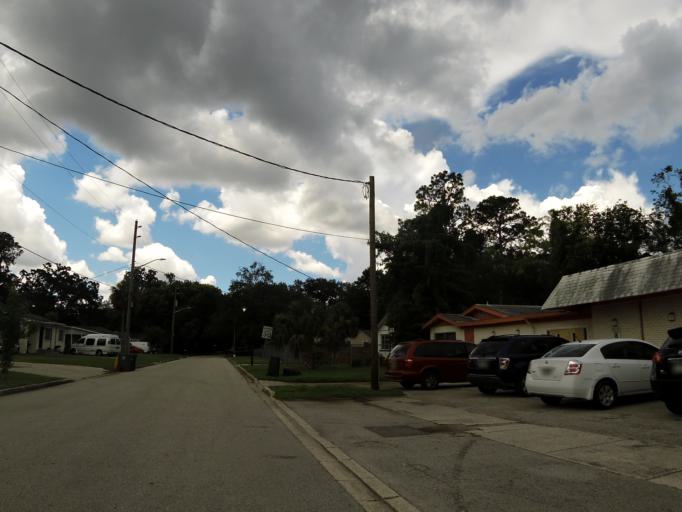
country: US
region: Florida
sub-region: Duval County
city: Jacksonville
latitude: 30.3039
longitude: -81.6320
